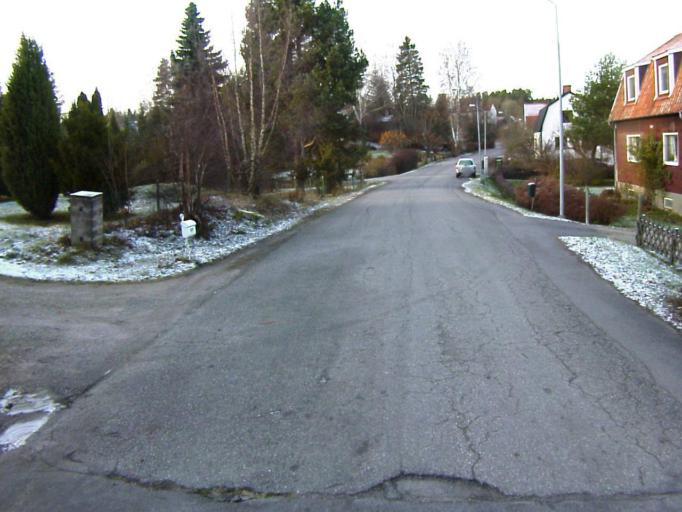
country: SE
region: Soedermanland
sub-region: Eskilstuna Kommun
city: Hallbybrunn
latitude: 59.3907
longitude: 16.4372
